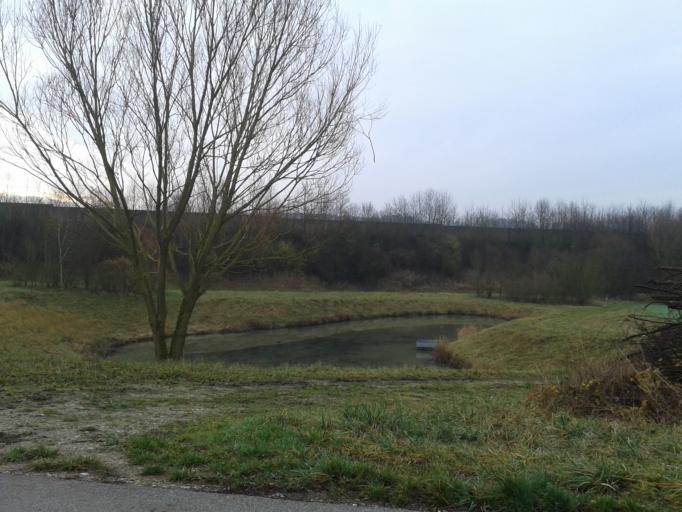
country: DE
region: Bavaria
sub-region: Upper Franconia
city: Memmelsdorf
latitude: 49.9422
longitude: 10.9608
